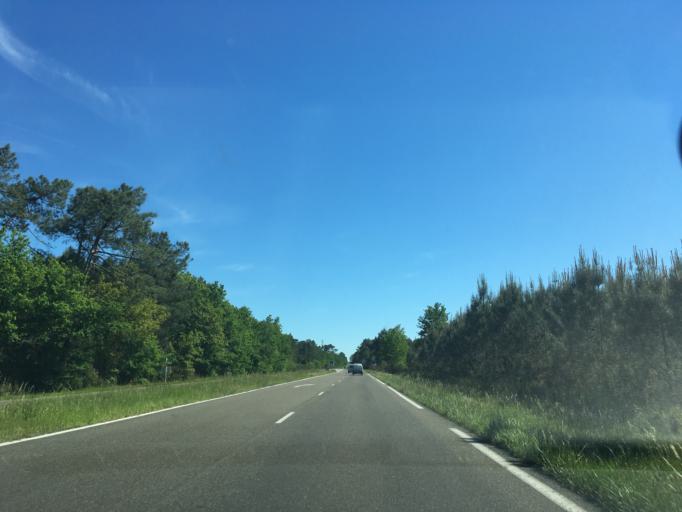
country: FR
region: Aquitaine
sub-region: Departement de la Gironde
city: Listrac-Medoc
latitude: 45.1031
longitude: -0.8035
